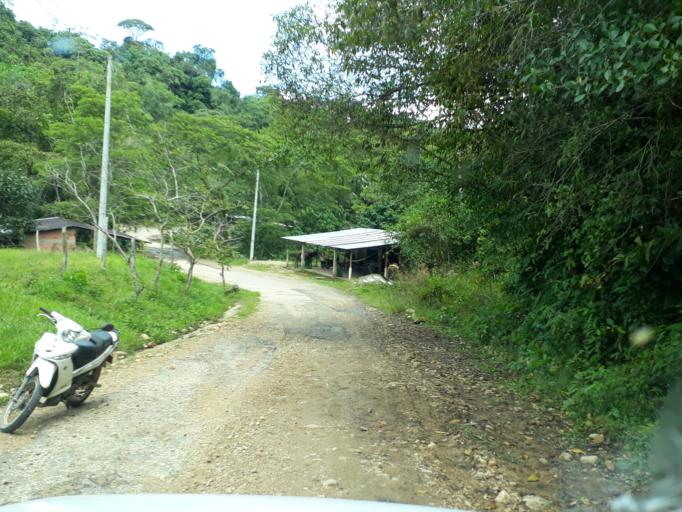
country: CO
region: Cundinamarca
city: Medina
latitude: 4.5945
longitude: -73.2981
